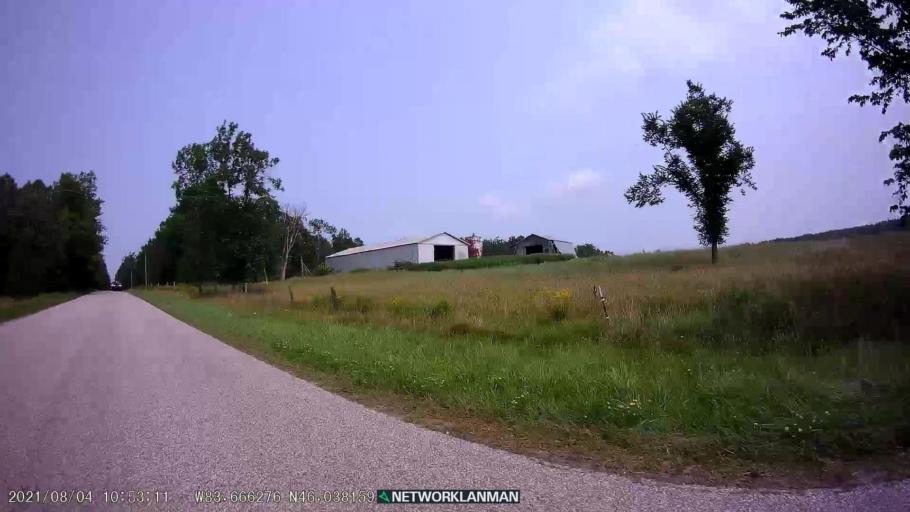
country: CA
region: Ontario
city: Thessalon
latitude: 46.0391
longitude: -83.6663
